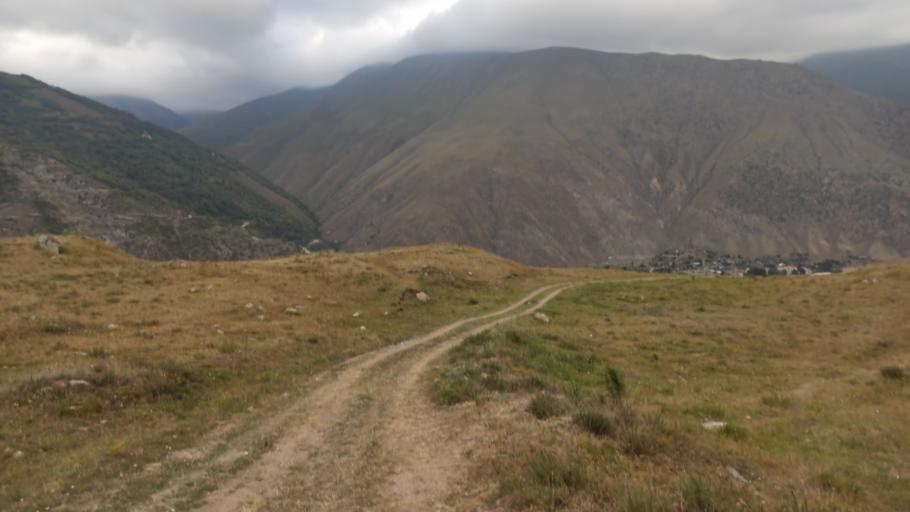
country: RU
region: Kabardino-Balkariya
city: Tyrnyauz
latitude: 43.3907
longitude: 42.9268
